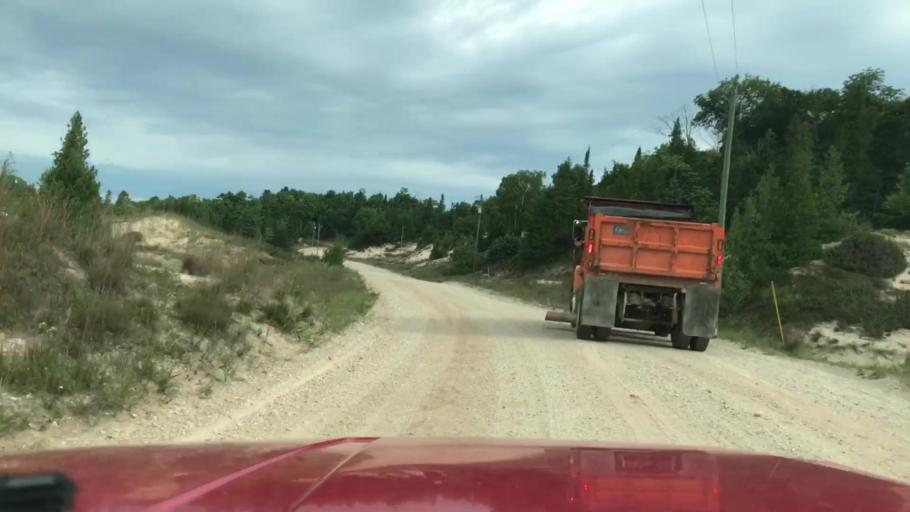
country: US
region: Michigan
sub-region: Charlevoix County
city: Charlevoix
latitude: 45.7383
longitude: -85.5593
